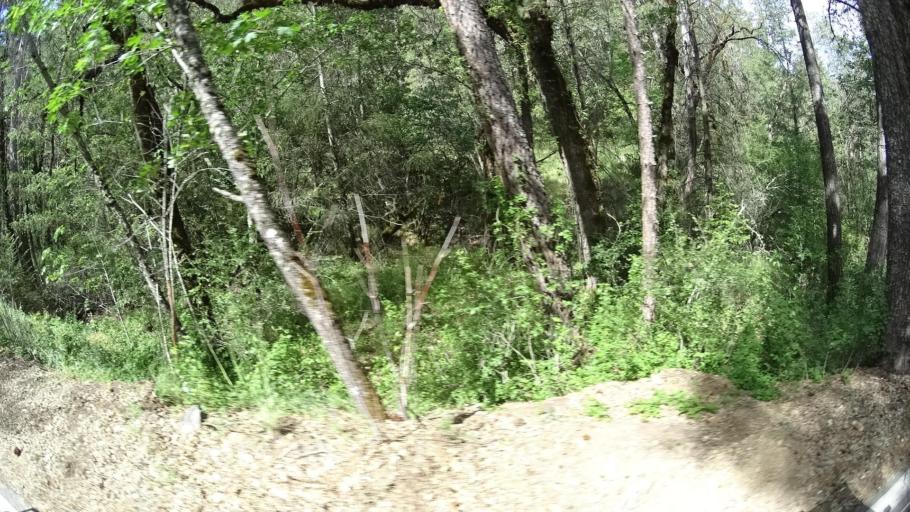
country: US
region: California
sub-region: Lake County
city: Cobb
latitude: 38.8574
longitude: -122.7407
